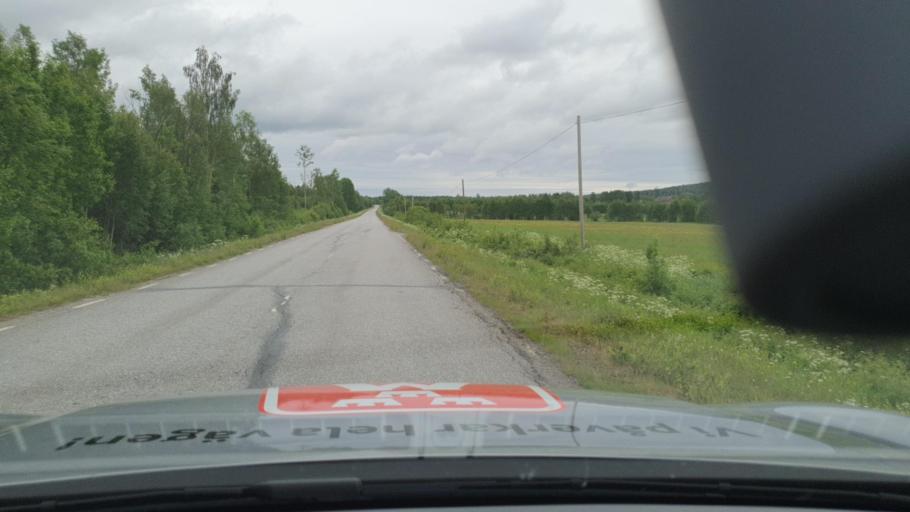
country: SE
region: Norrbotten
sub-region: Lulea Kommun
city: Ranea
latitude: 65.8508
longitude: 22.2444
